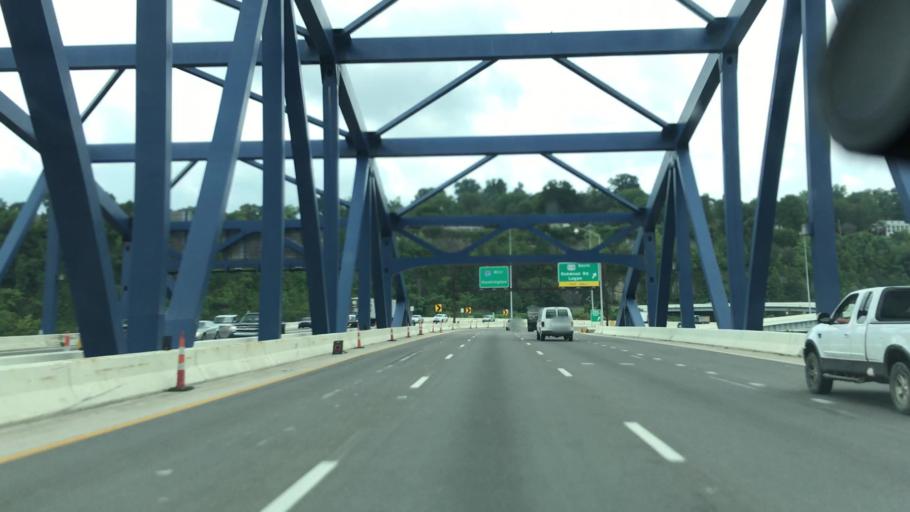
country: US
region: West Virginia
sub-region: Kanawha County
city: Charleston
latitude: 38.3555
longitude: -81.6489
